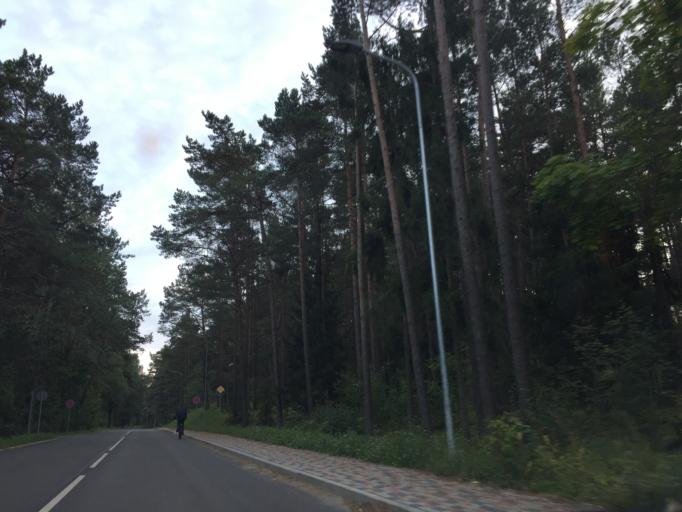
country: LV
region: Saulkrastu
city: Saulkrasti
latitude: 57.3228
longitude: 24.4099
